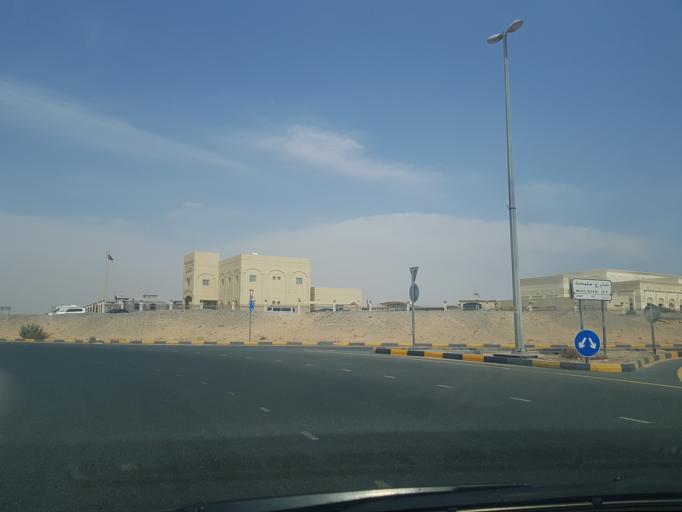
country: AE
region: Ash Shariqah
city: Sharjah
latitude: 25.2269
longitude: 55.6006
